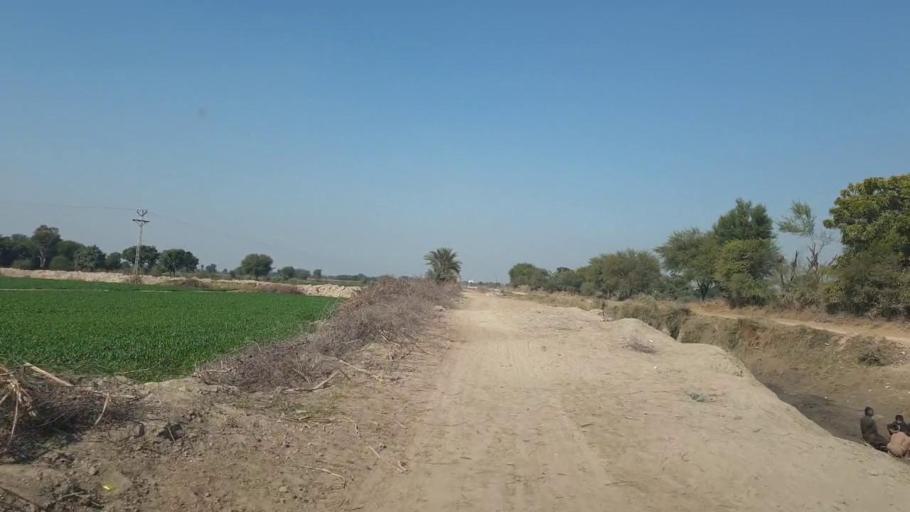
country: PK
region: Sindh
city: Shahdadpur
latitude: 25.9466
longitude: 68.6339
